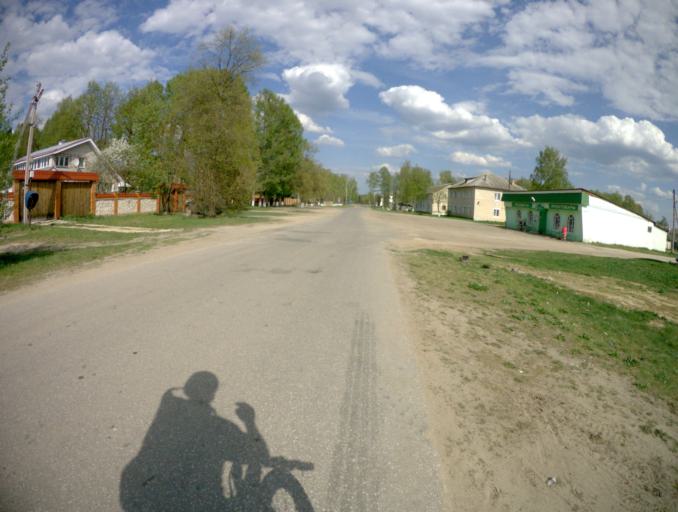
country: RU
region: Vladimir
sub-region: Kovrovskiy Rayon
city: Kovrov
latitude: 56.4419
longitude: 41.2961
